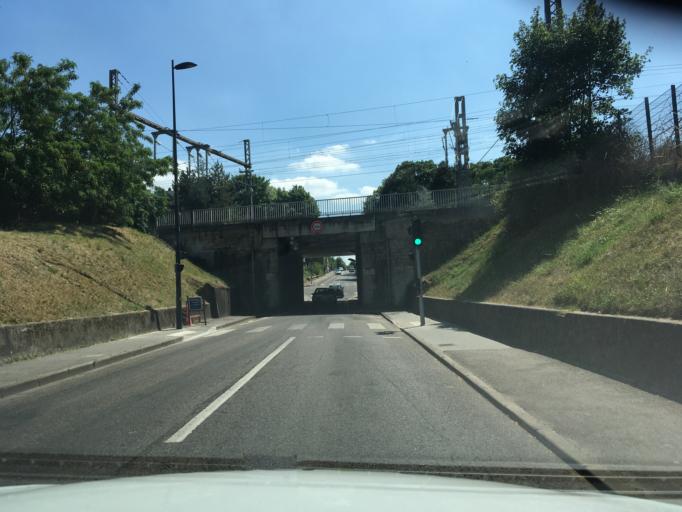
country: FR
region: Lorraine
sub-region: Departement de Meurthe-et-Moselle
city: Jarville-la-Malgrange
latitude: 48.6715
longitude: 6.2008
